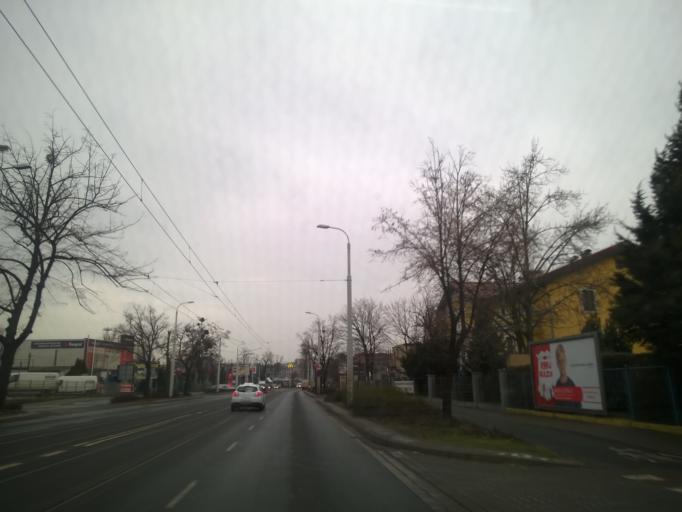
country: PL
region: Lower Silesian Voivodeship
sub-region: Powiat wroclawski
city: Wroclaw
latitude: 51.0939
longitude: 17.0594
